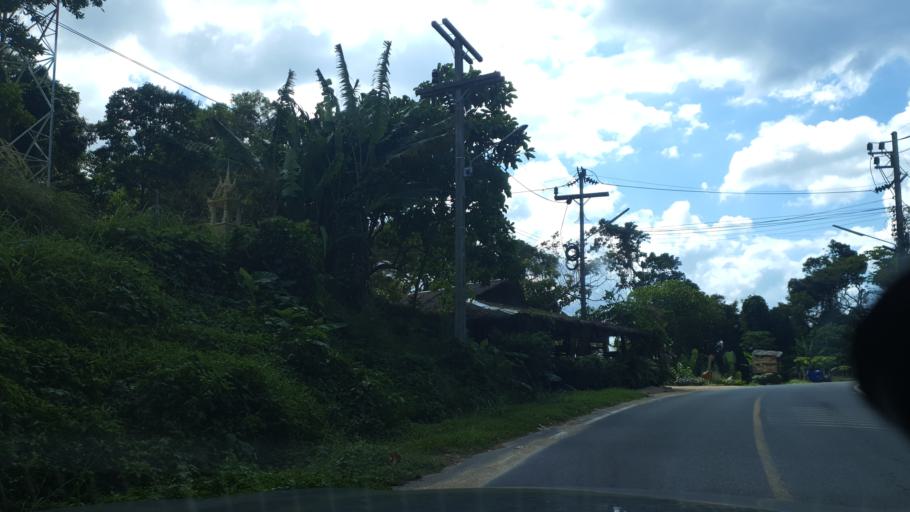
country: TH
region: Phuket
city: Thalang
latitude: 8.0638
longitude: 98.2872
